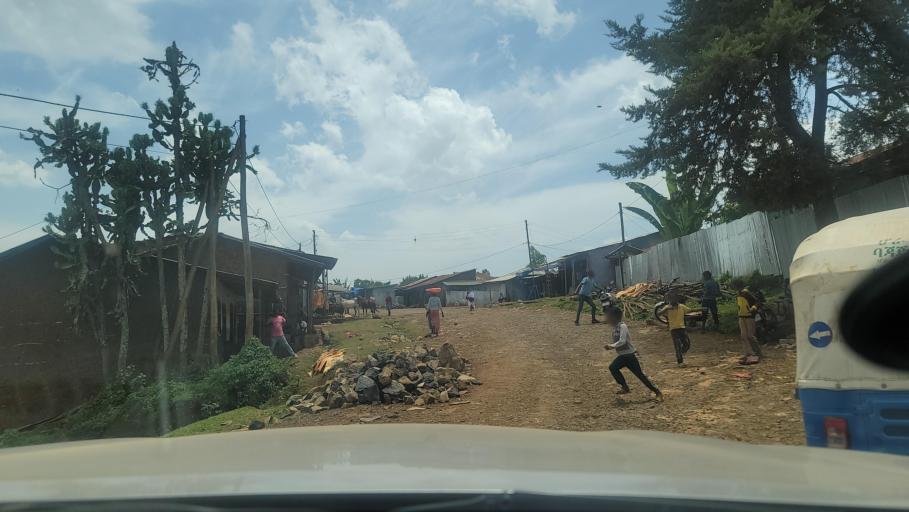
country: ET
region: Oromiya
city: Agaro
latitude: 7.7392
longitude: 36.2535
